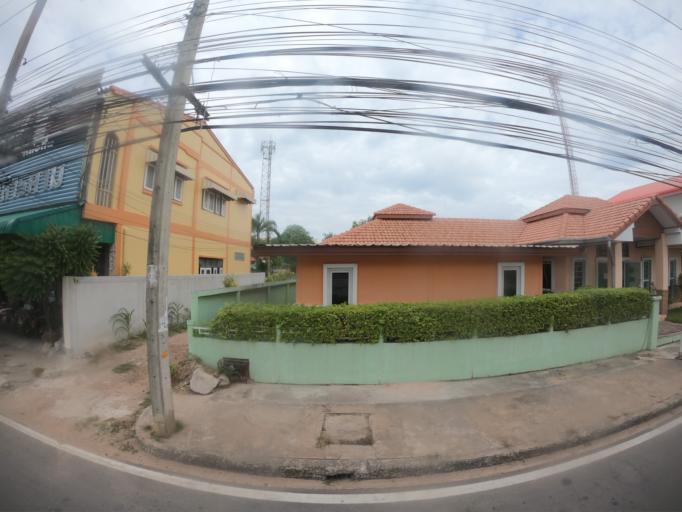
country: TH
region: Maha Sarakham
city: Maha Sarakham
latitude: 16.1794
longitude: 103.3076
